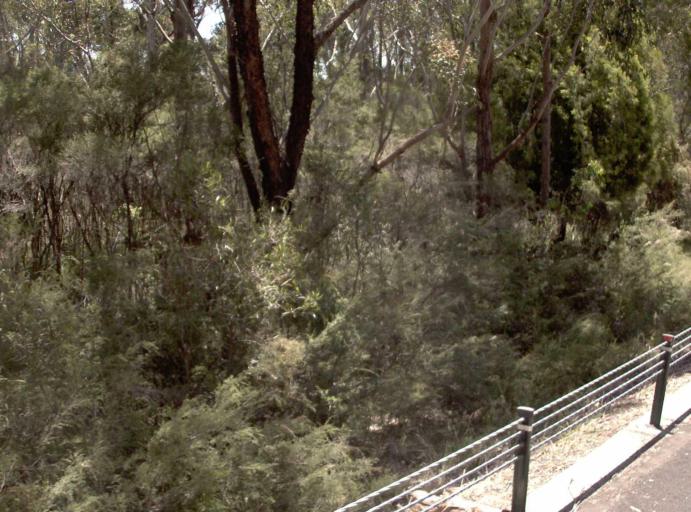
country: AU
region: Victoria
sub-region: East Gippsland
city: Lakes Entrance
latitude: -37.7469
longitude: 148.0720
